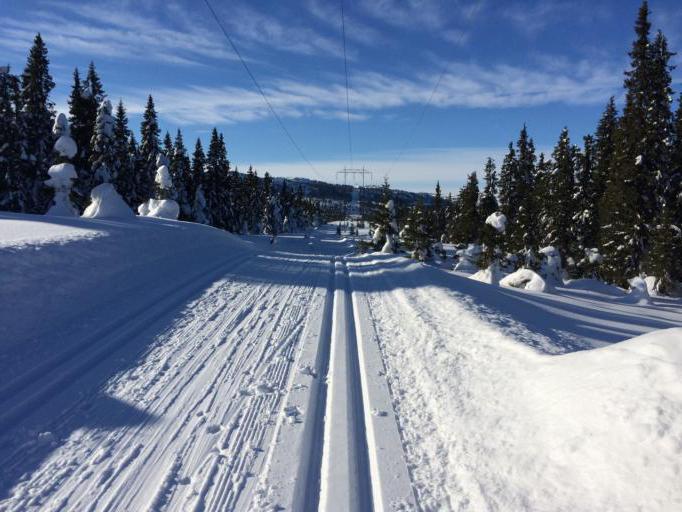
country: NO
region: Oppland
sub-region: Gausdal
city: Segalstad bru
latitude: 61.3192
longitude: 10.0906
